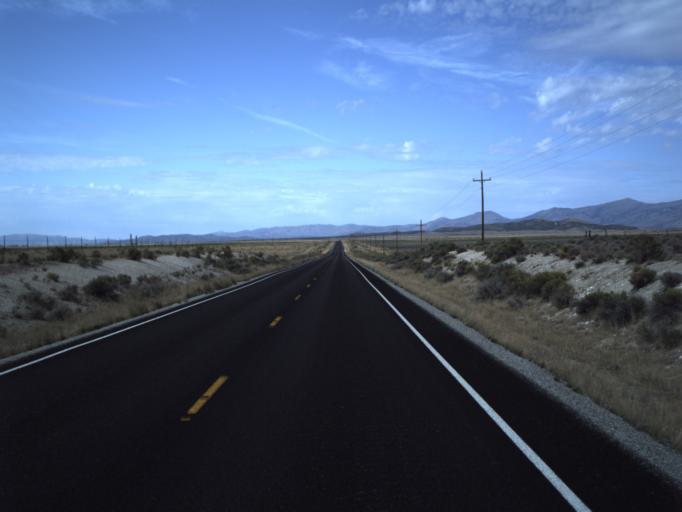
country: US
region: Idaho
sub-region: Cassia County
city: Burley
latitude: 41.7774
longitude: -113.4915
